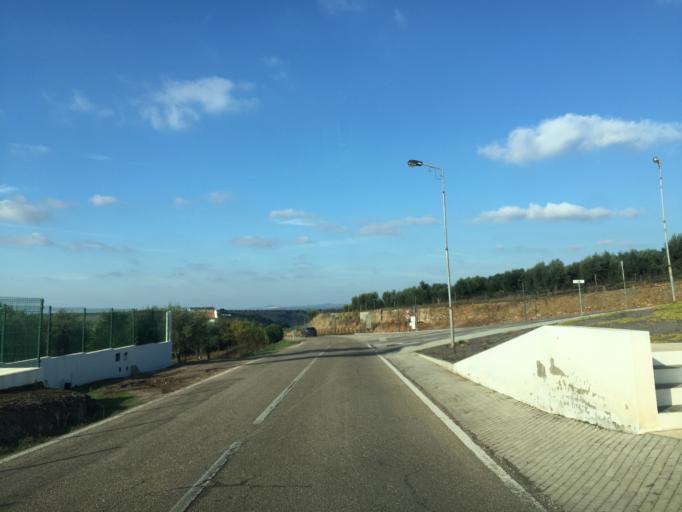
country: PT
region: Portalegre
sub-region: Fronteira
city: Fronteira
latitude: 39.0622
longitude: -7.6512
